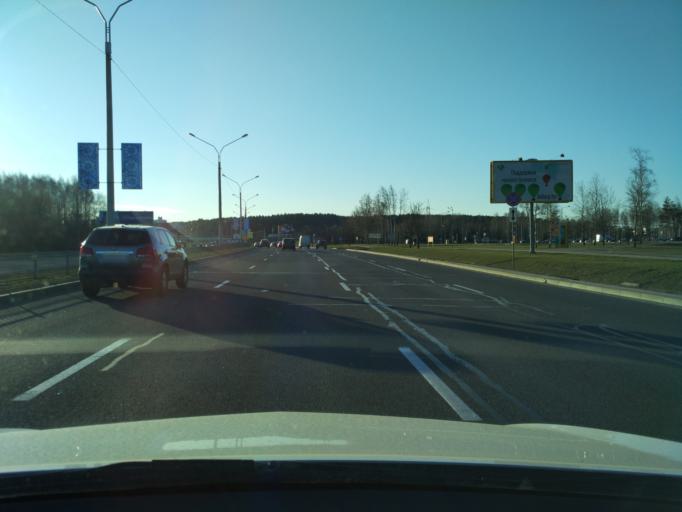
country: BY
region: Minsk
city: Zhdanovichy
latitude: 53.9483
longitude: 27.4529
